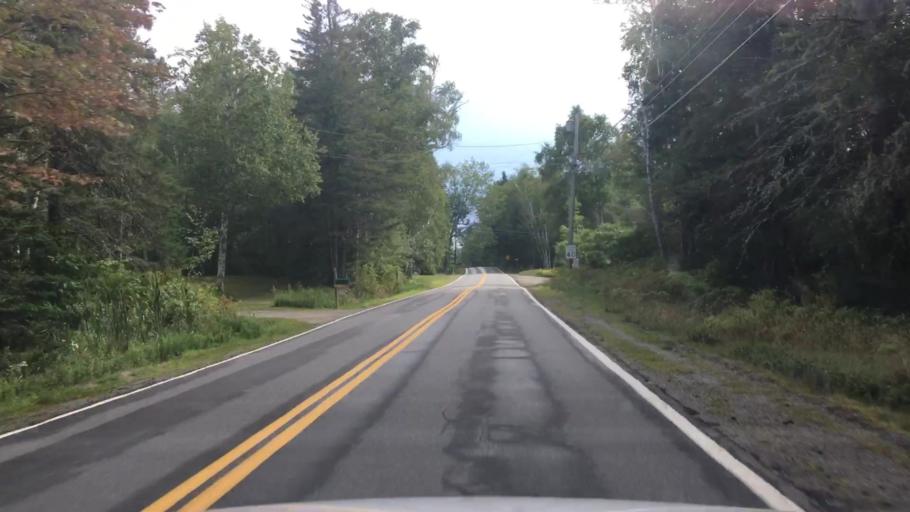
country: US
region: Maine
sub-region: Hancock County
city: Ellsworth
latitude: 44.4820
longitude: -68.4204
